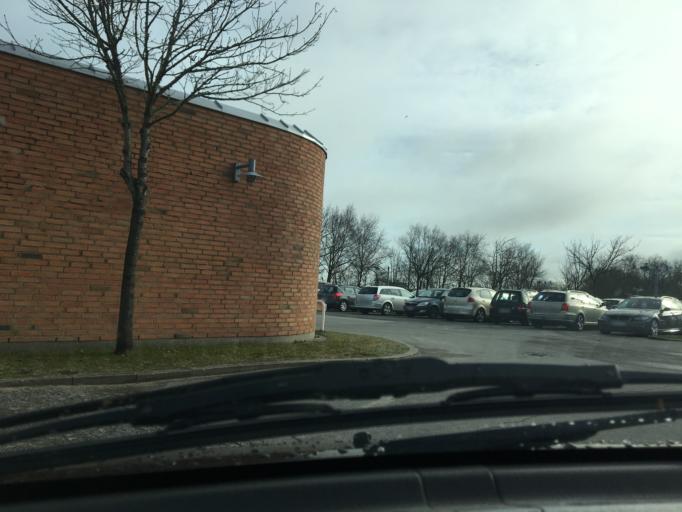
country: DK
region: North Denmark
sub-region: Alborg Kommune
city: Gistrup
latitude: 57.0123
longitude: 9.9921
